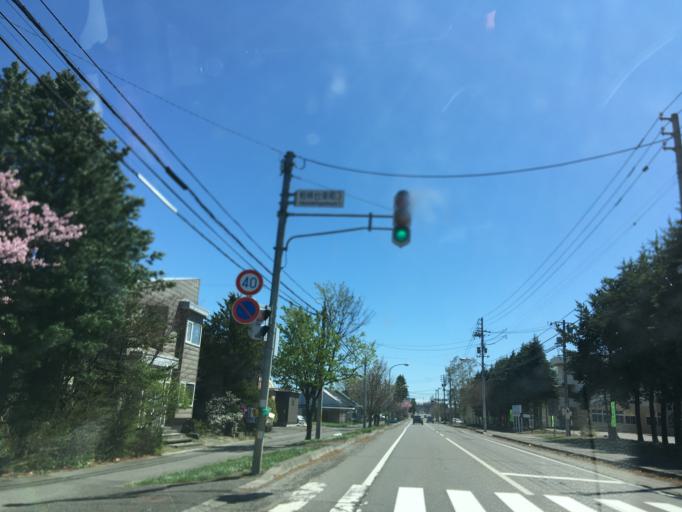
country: JP
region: Hokkaido
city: Obihiro
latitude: 42.9230
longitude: 143.1712
